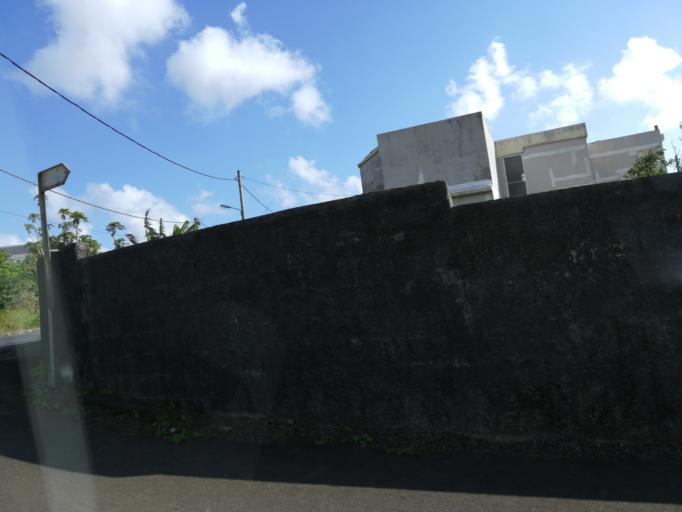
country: MU
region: Moka
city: Verdun
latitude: -20.2231
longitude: 57.5462
